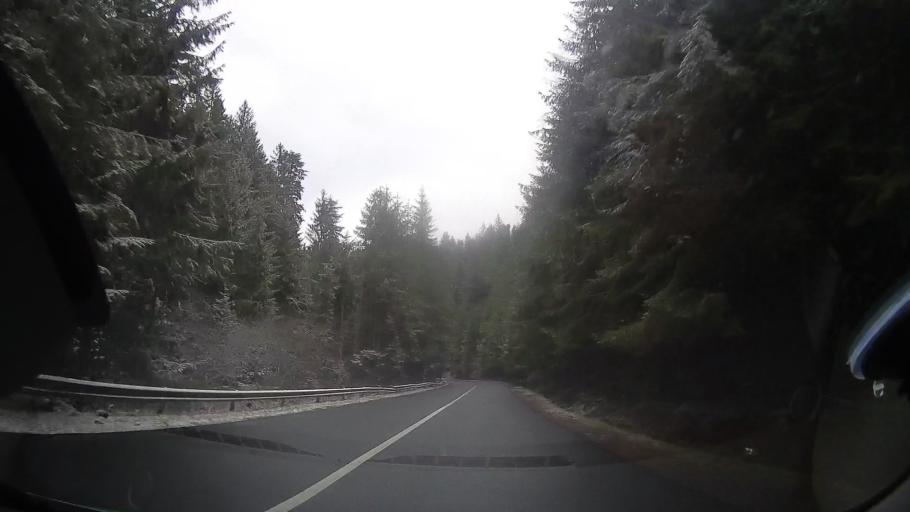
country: RO
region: Cluj
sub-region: Comuna Calatele
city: Calatele
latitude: 46.7371
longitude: 23.0386
